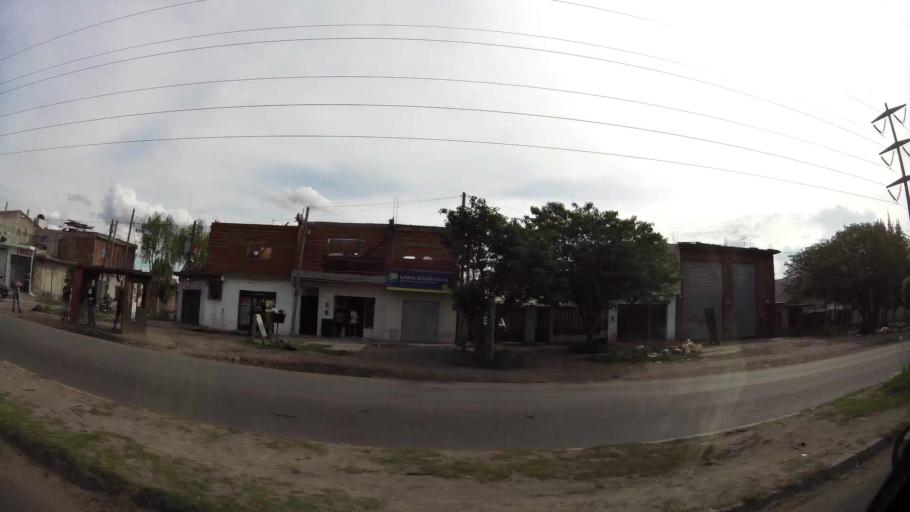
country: AR
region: Buenos Aires
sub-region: Partido de Quilmes
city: Quilmes
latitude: -34.7620
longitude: -58.2526
